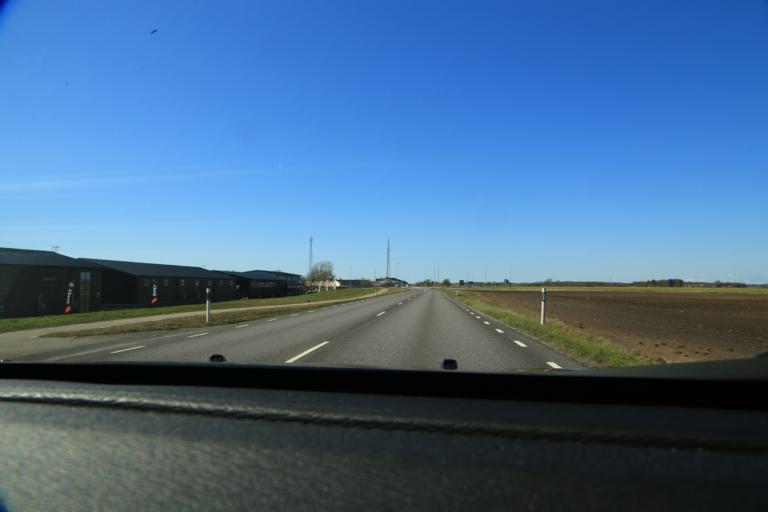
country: SE
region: Halland
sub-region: Varbergs Kommun
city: Traslovslage
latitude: 57.0546
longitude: 12.3017
